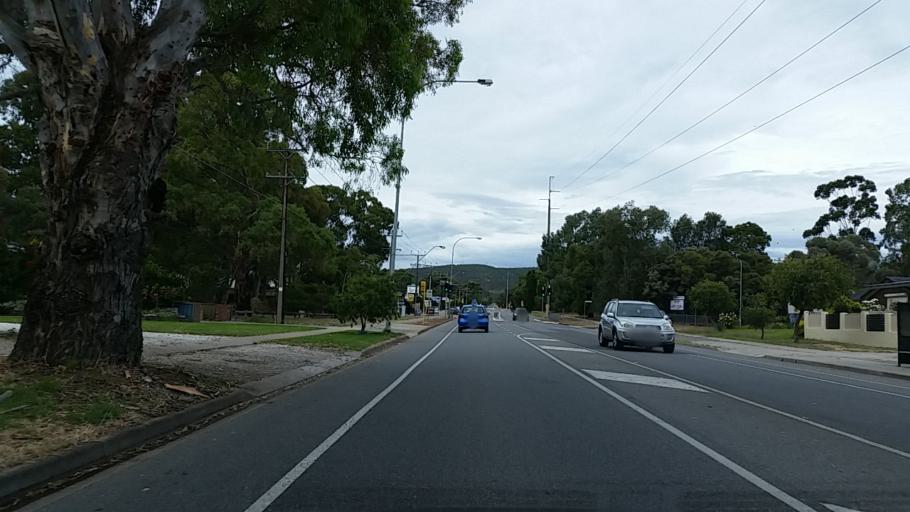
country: AU
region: South Australia
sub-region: Tea Tree Gully
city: Hope Valley
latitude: -34.8326
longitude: 138.7025
